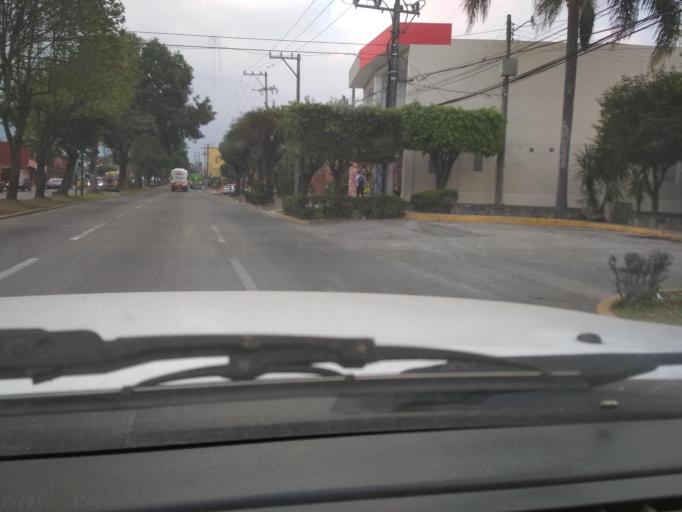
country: MX
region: Veracruz
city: Orizaba
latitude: 18.8638
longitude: -97.1003
